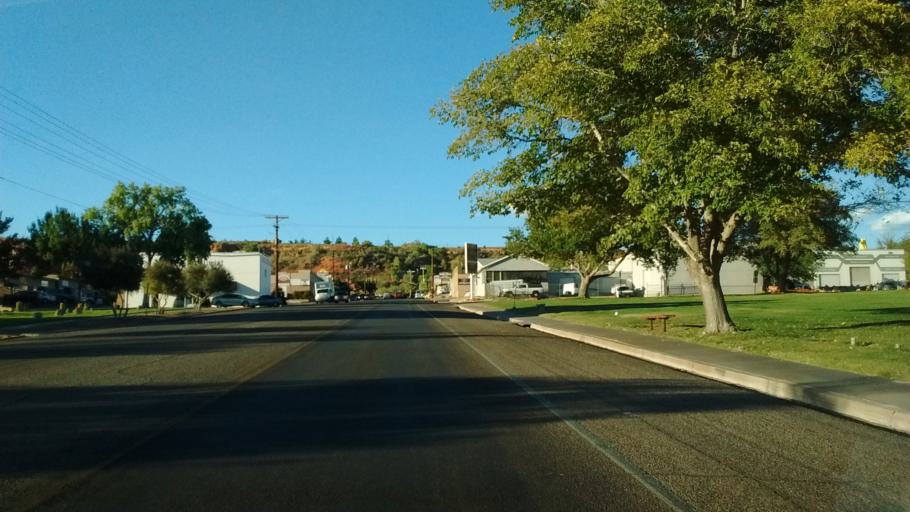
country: US
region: Utah
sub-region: Washington County
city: Saint George
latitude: 37.1073
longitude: -113.5685
